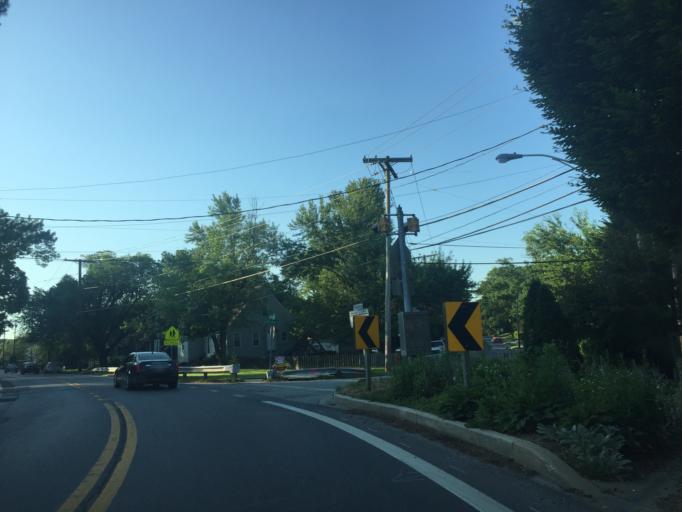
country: US
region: Maryland
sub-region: Baltimore County
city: Catonsville
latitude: 39.2674
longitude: -76.7455
